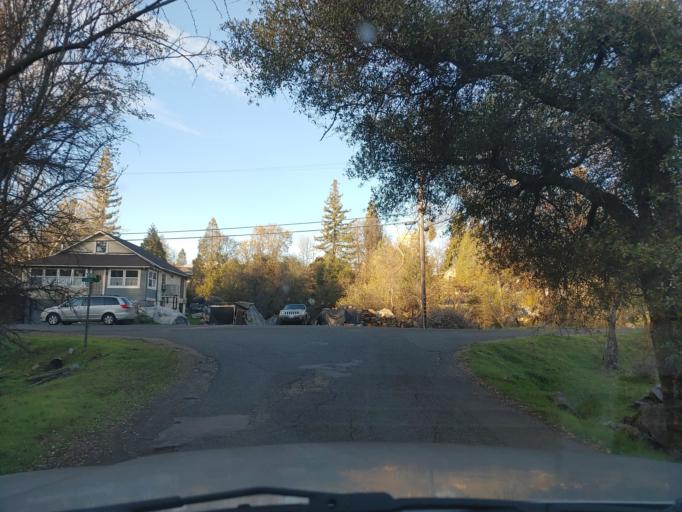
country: US
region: California
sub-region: Tuolumne County
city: Columbia
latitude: 38.0348
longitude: -120.4028
